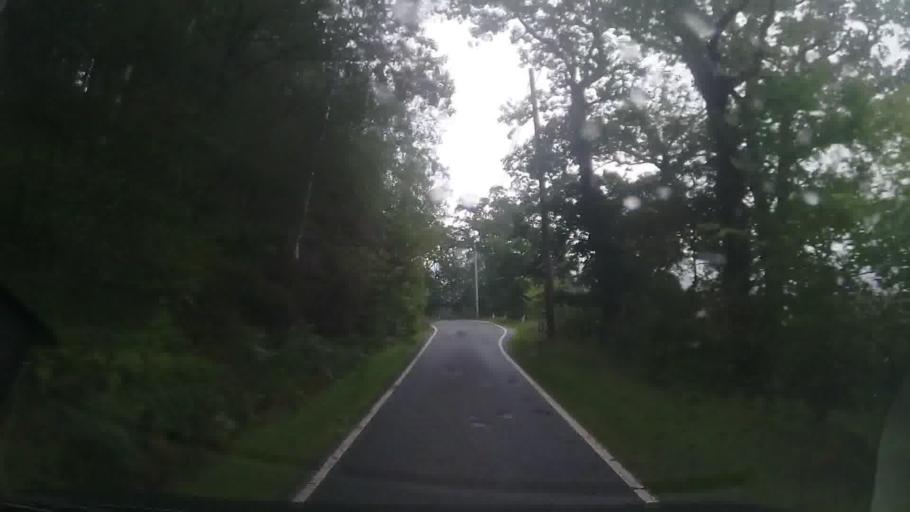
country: GB
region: Scotland
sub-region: Argyll and Bute
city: Isle Of Mull
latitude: 56.7108
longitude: -5.7650
